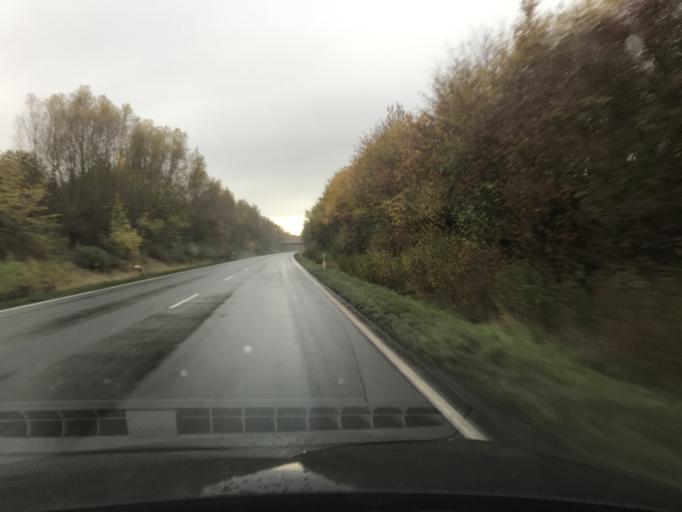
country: DE
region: North Rhine-Westphalia
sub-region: Regierungsbezirk Arnsberg
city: Hamm
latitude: 51.7059
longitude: 7.7388
